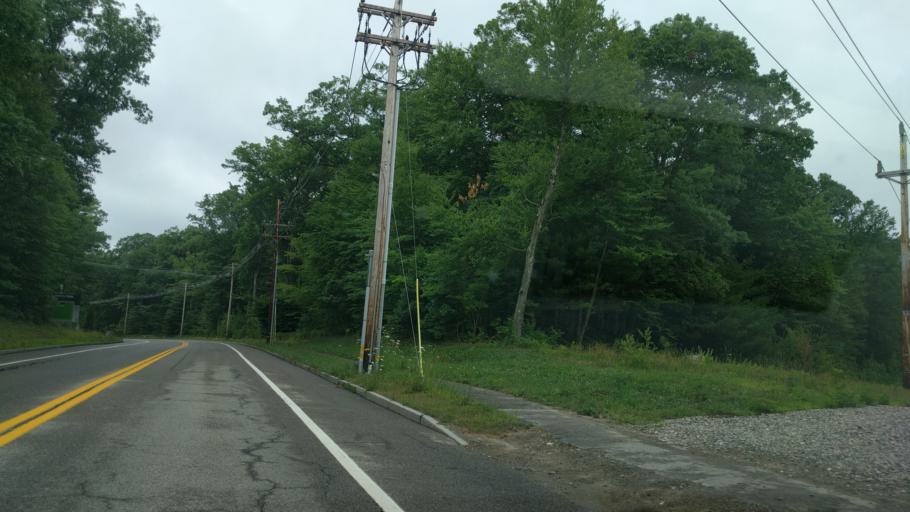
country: US
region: Massachusetts
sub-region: Worcester County
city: Shrewsbury
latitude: 42.2554
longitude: -71.6897
